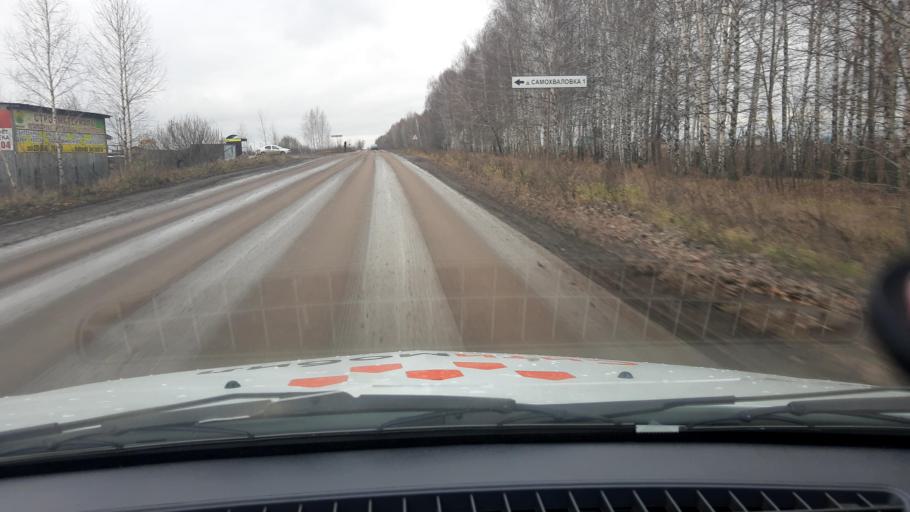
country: RU
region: Bashkortostan
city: Kabakovo
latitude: 54.6799
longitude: 56.1329
